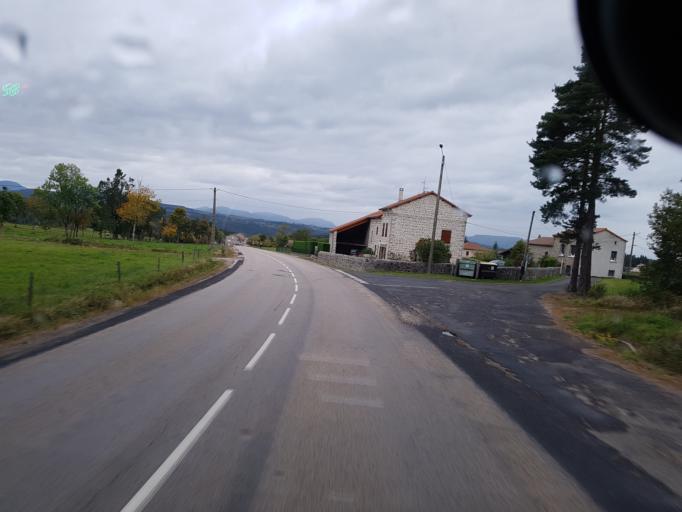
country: FR
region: Auvergne
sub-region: Departement de la Haute-Loire
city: Sainte-Sigolene
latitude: 45.2336
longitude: 4.2138
